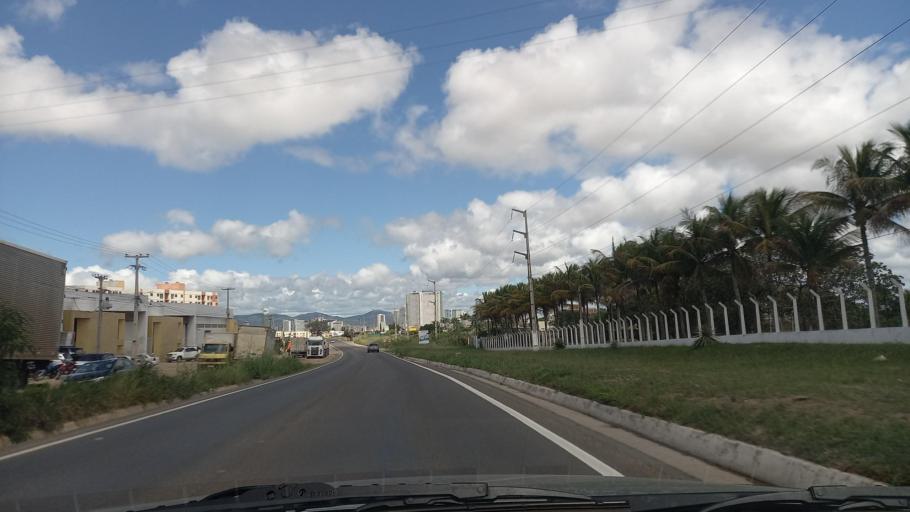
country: BR
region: Pernambuco
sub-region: Caruaru
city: Caruaru
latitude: -8.2544
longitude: -35.9510
